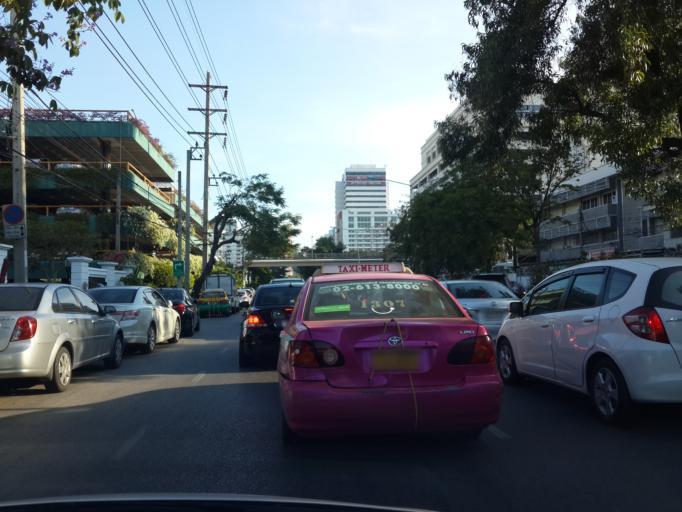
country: TH
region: Bangkok
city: Pathum Wan
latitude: 13.7403
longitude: 100.5351
